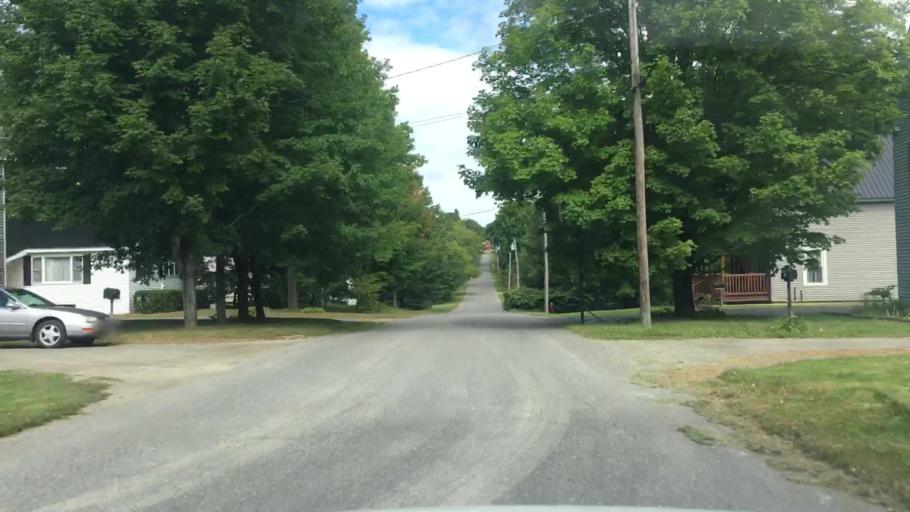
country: US
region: Maine
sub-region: Piscataquis County
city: Dover-Foxcroft
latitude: 45.1872
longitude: -69.2221
